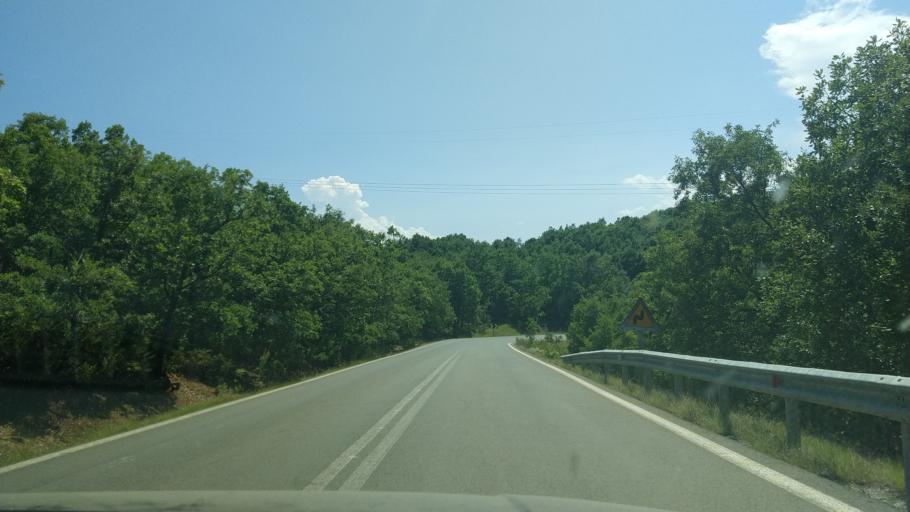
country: GR
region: West Macedonia
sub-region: Nomos Grevenon
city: Grevena
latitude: 40.0340
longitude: 21.4823
